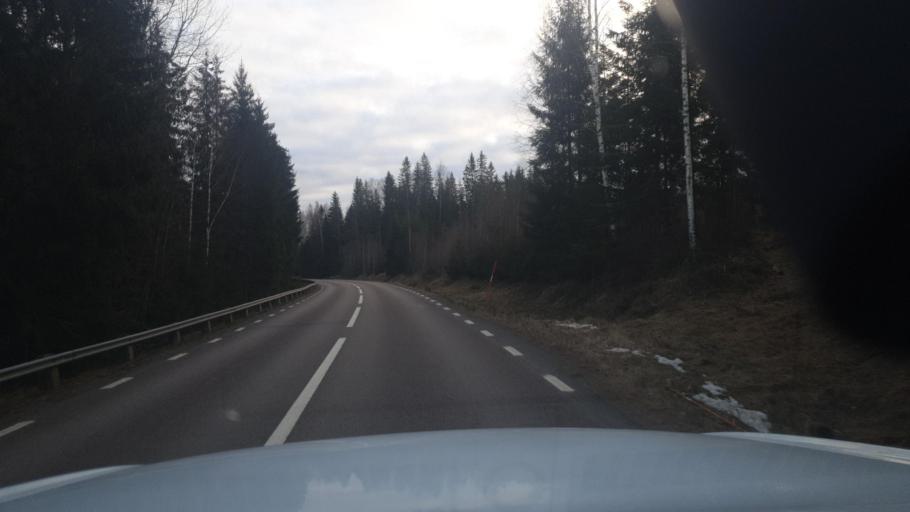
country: SE
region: Vaermland
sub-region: Sunne Kommun
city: Sunne
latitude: 59.9044
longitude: 12.9069
